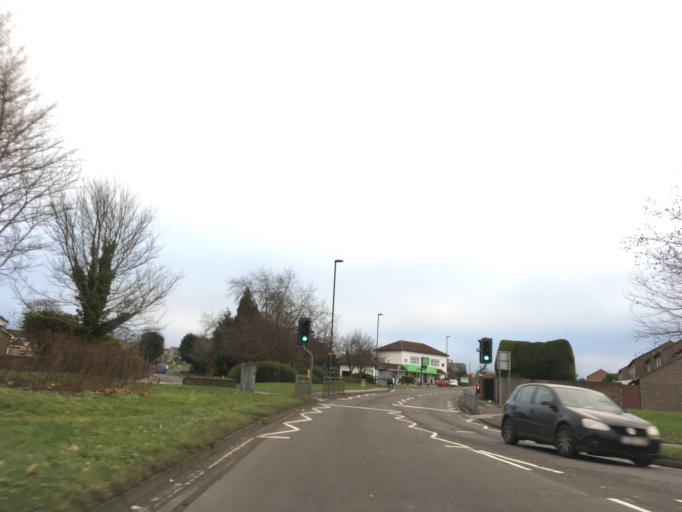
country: GB
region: England
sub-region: South Gloucestershire
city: Stoke Gifford
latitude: 51.5174
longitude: -2.5471
